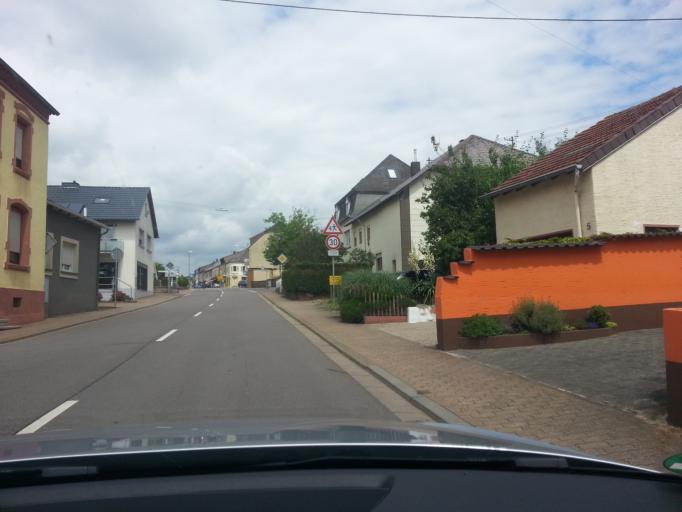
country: DE
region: Saarland
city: Orscholz
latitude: 49.5043
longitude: 6.5236
